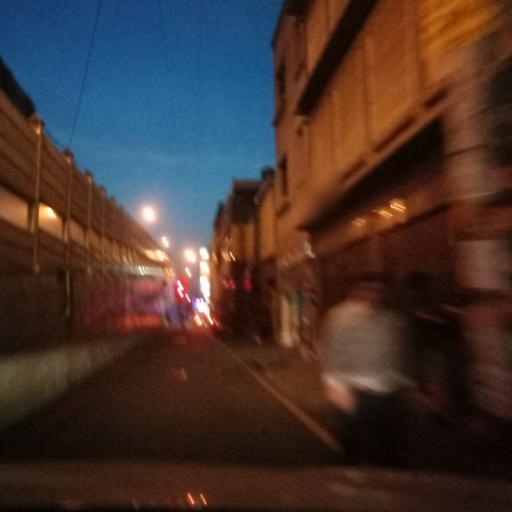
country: TW
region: Taiwan
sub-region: Hsinchu
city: Zhubei
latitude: 24.9036
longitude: 121.0458
